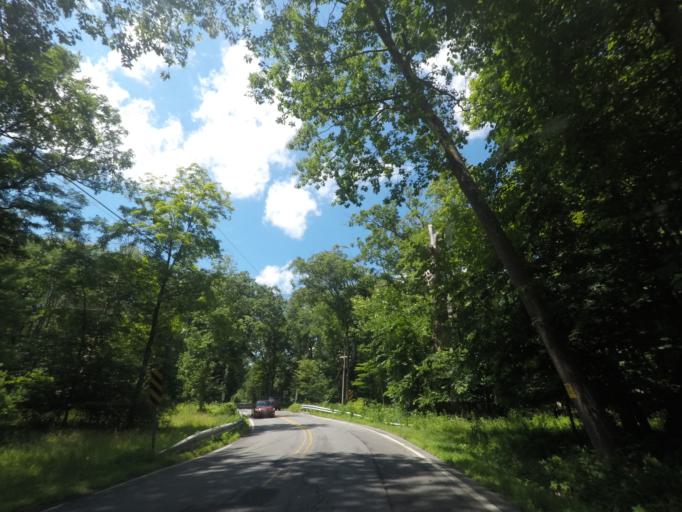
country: US
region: New York
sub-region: Albany County
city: Westmere
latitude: 42.6896
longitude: -73.9063
